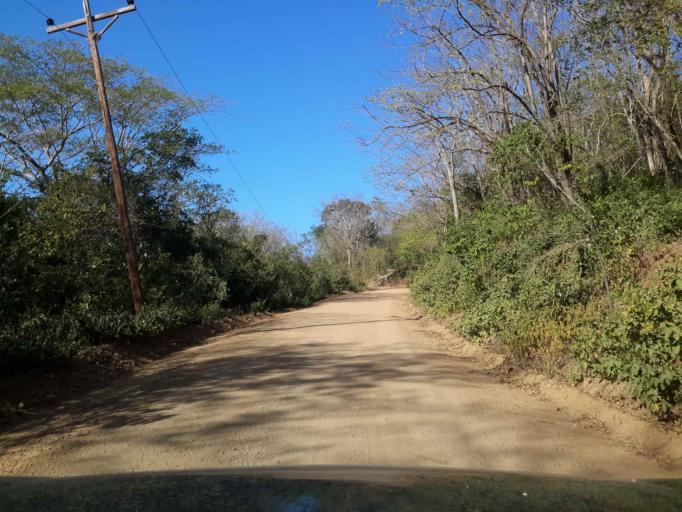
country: NI
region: Rivas
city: San Juan del Sur
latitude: 11.1824
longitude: -85.7997
